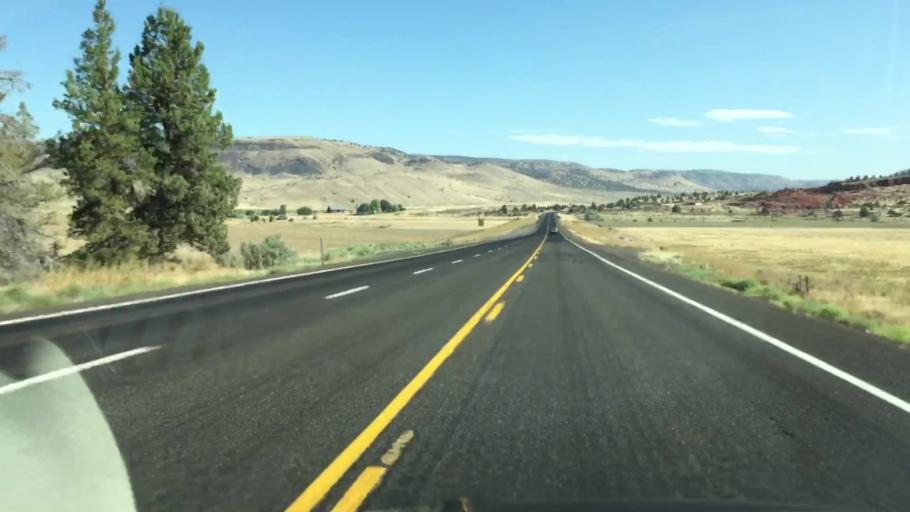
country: US
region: Oregon
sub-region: Jefferson County
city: Madras
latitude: 44.7694
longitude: -120.9706
